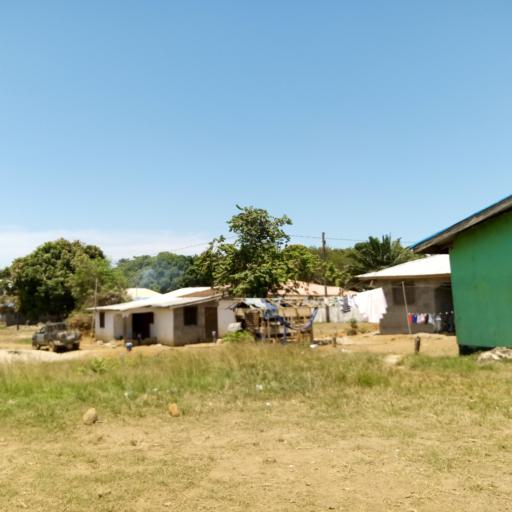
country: LR
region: Montserrado
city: Monrovia
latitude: 6.2517
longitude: -10.6887
